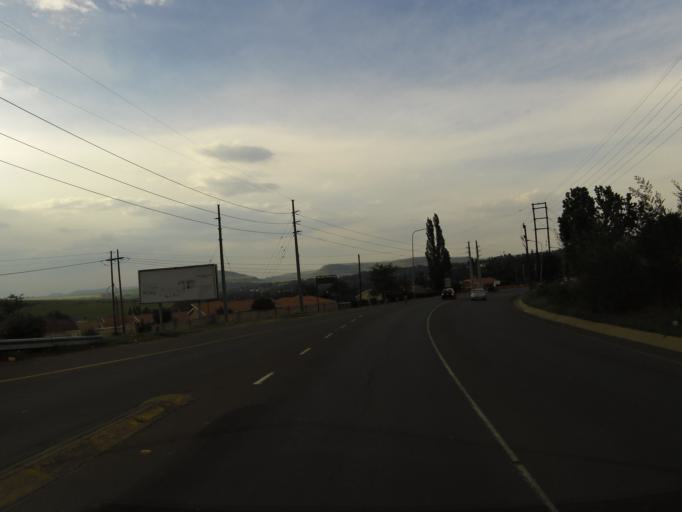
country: LS
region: Maseru
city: Maseru
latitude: -29.3248
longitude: 27.4726
